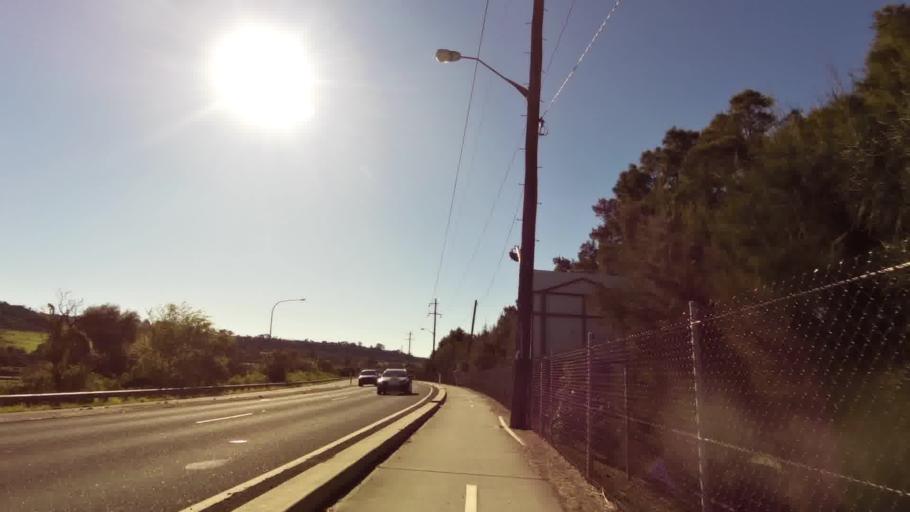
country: AU
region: New South Wales
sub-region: Wollongong
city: Koonawarra
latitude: -34.4739
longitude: 150.8137
